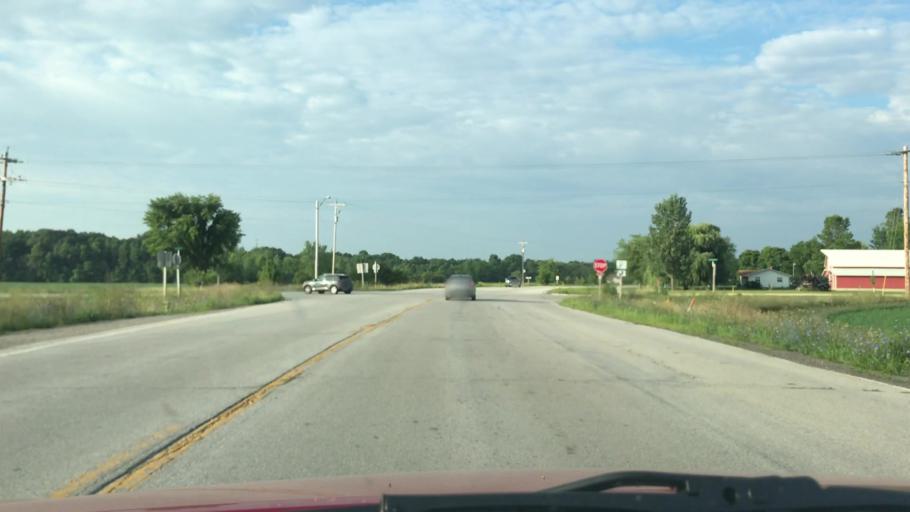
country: US
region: Wisconsin
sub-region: Brown County
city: De Pere
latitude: 44.4306
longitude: -88.1359
